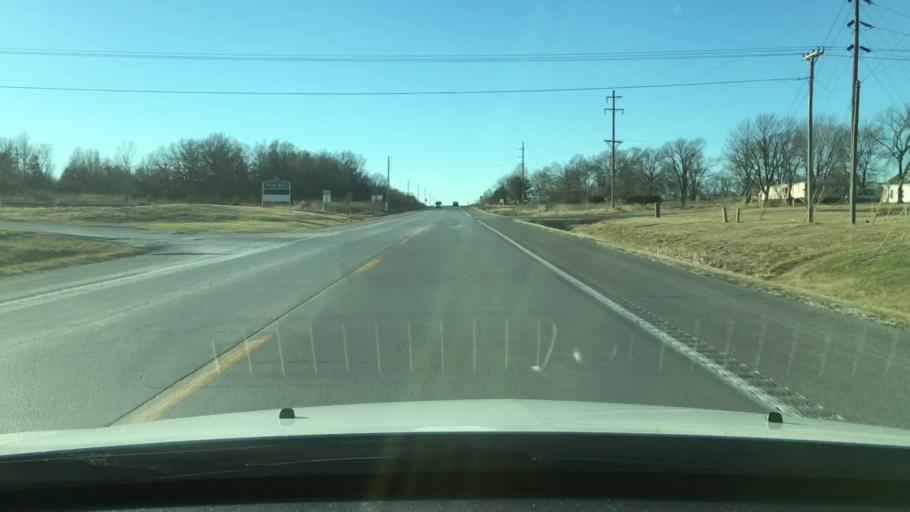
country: US
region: Missouri
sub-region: Audrain County
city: Mexico
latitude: 39.1858
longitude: -91.9374
